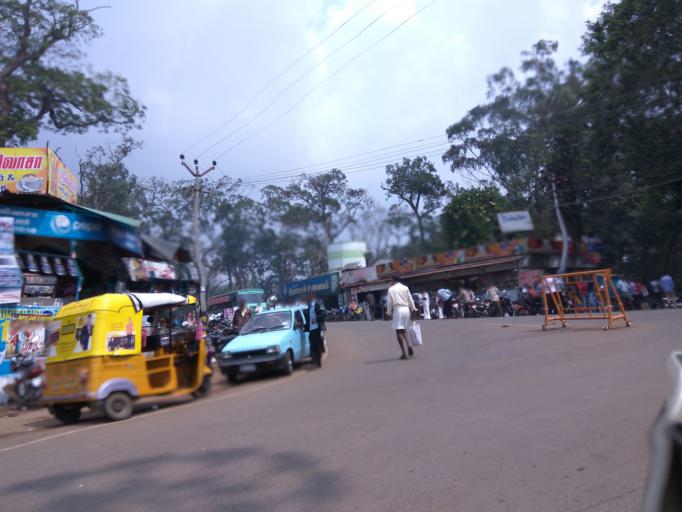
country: IN
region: Tamil Nadu
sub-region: Salem
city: Salem
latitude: 11.7856
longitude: 78.2110
